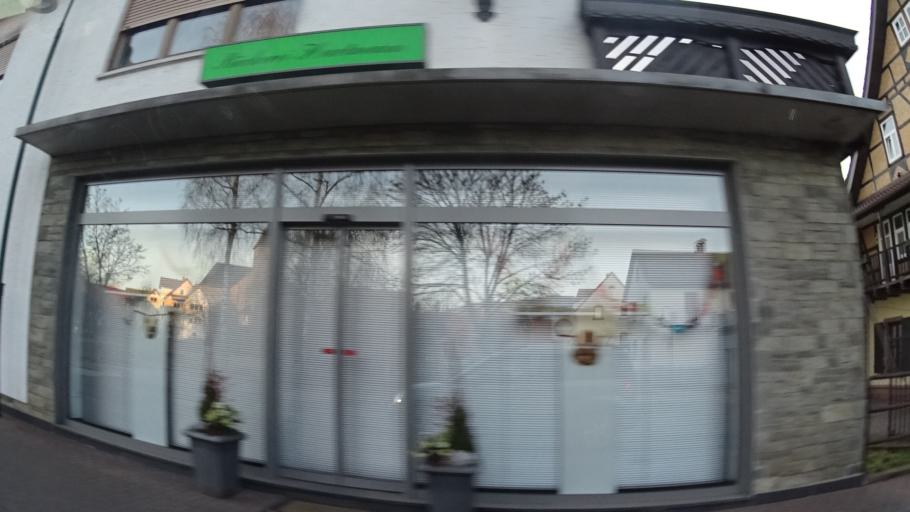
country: DE
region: Bavaria
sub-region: Regierungsbezirk Unterfranken
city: Geiselbach
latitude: 50.1220
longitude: 9.1988
